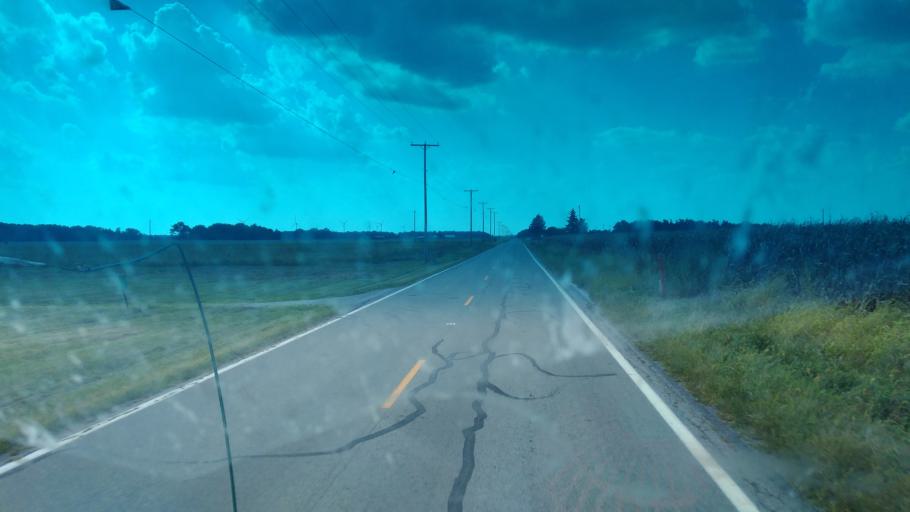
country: US
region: Ohio
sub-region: Hancock County
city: Arlington
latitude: 40.7796
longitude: -83.6686
